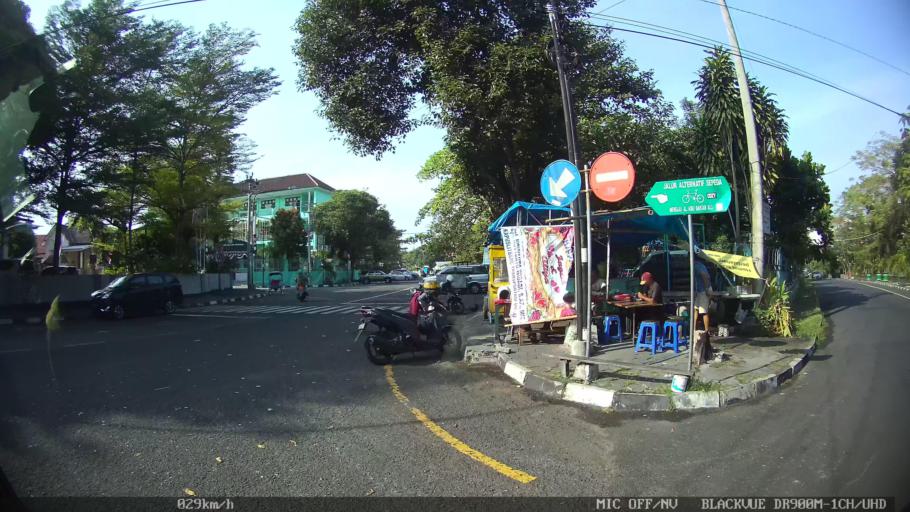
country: ID
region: Daerah Istimewa Yogyakarta
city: Yogyakarta
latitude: -7.7858
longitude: 110.3694
